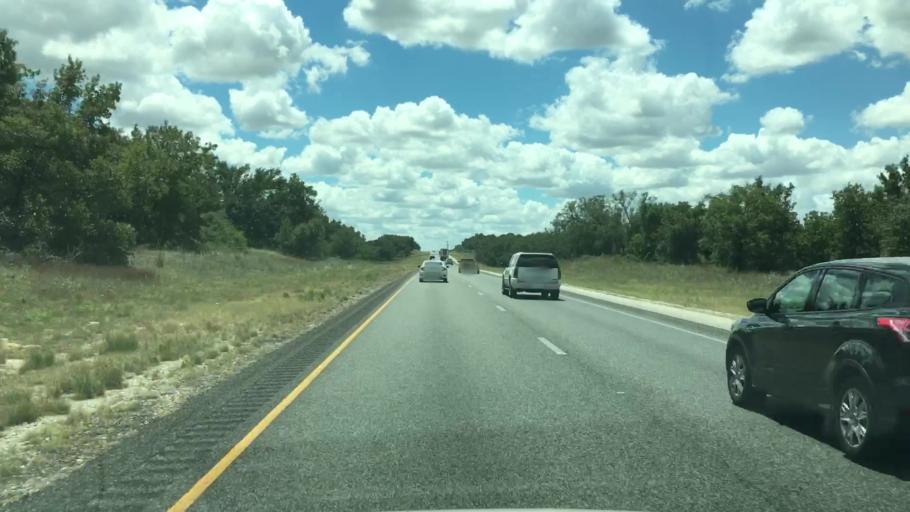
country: US
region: Texas
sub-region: Bexar County
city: Elmendorf
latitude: 29.1955
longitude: -98.4217
